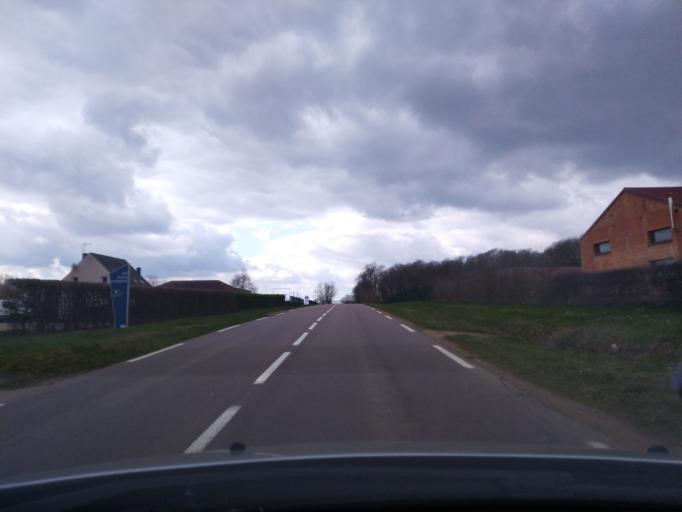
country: FR
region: Bourgogne
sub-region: Departement de l'Yonne
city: Avallon
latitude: 47.5078
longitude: 3.9347
